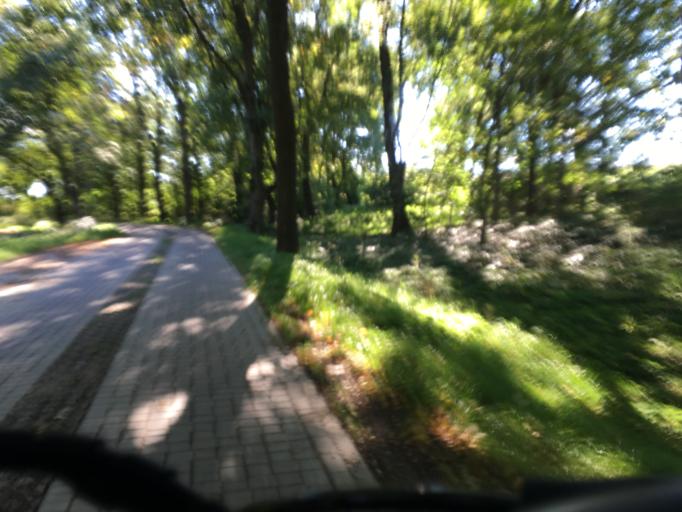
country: DE
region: Lower Saxony
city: Bardowick
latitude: 53.3049
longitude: 10.3786
